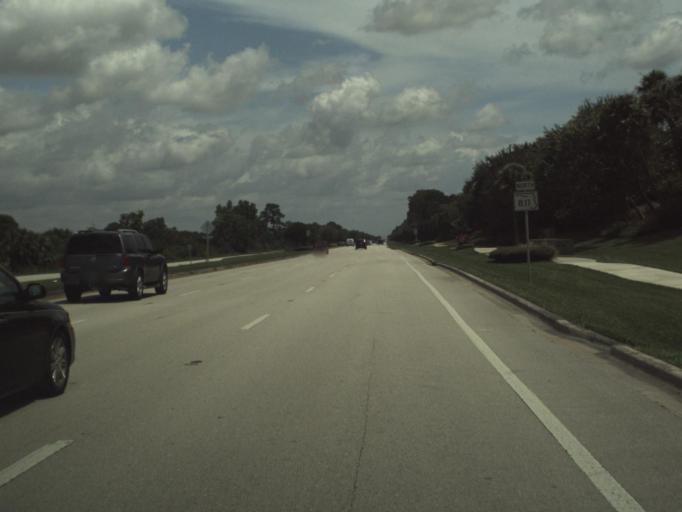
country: US
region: Florida
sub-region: Palm Beach County
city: Juno Beach
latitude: 26.8645
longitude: -80.0957
